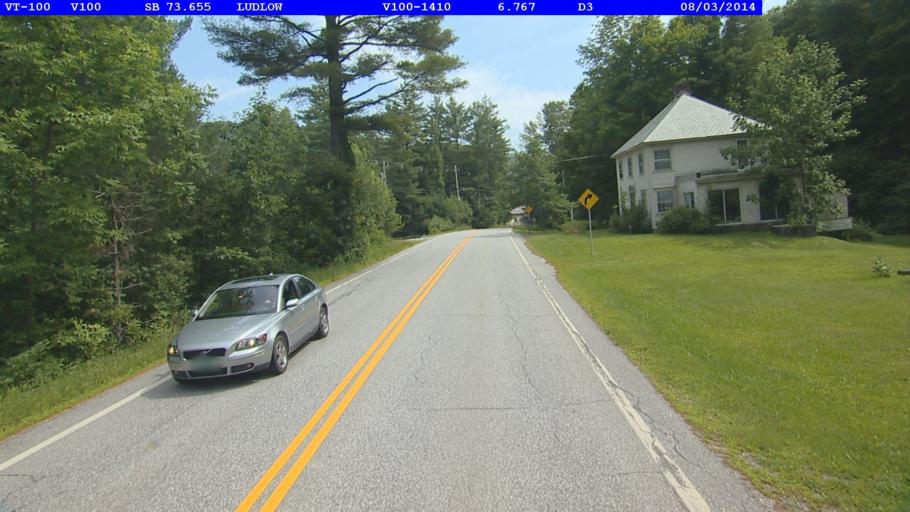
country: US
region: Vermont
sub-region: Windsor County
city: Chester
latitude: 43.4426
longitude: -72.6997
